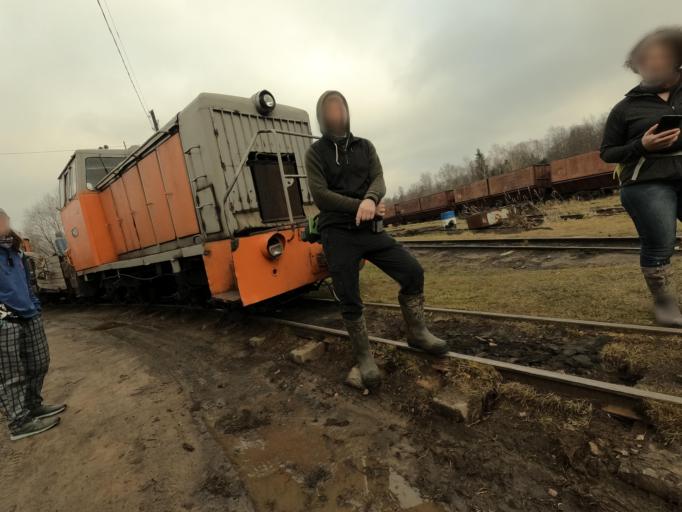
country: RU
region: Leningrad
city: Nurma
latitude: 59.5989
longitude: 31.2019
